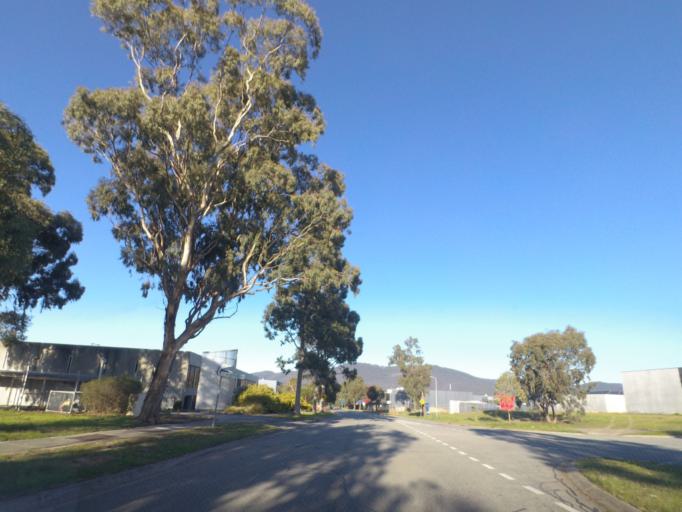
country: AU
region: Victoria
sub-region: Maroondah
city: Bayswater North
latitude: -37.8136
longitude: 145.2925
